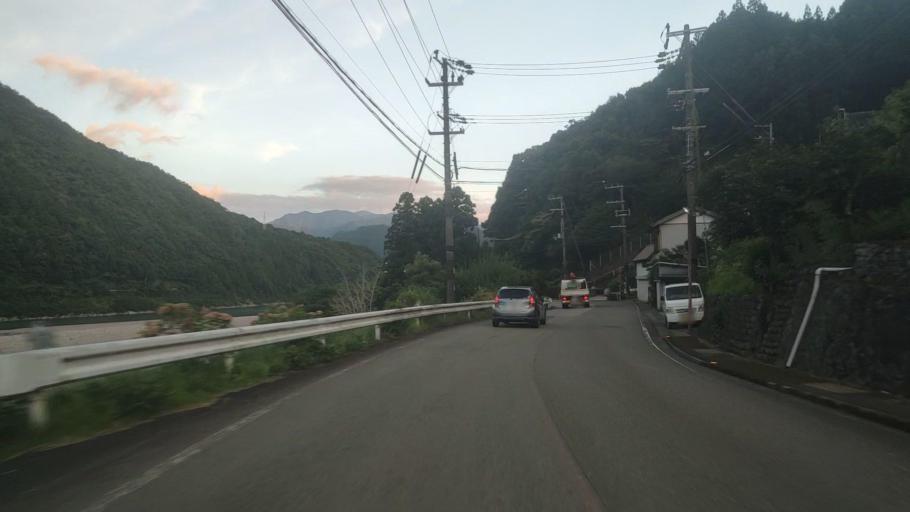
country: JP
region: Wakayama
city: Shingu
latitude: 33.8302
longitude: 135.8561
